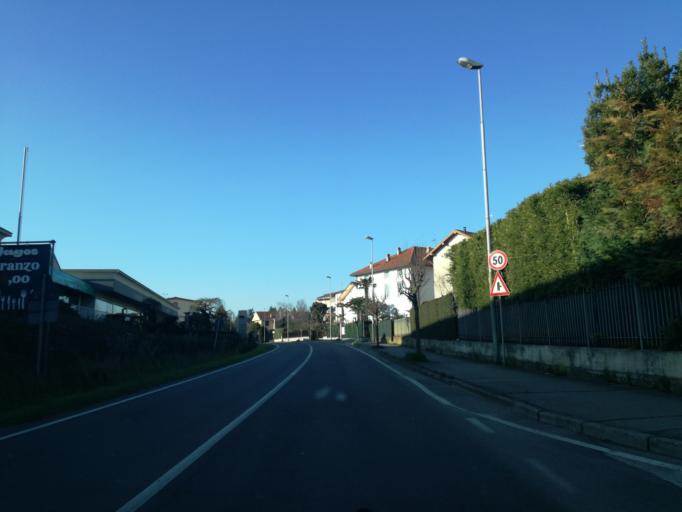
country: IT
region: Lombardy
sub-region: Provincia di Monza e Brianza
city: Ronco Briantino
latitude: 45.6578
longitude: 9.4141
